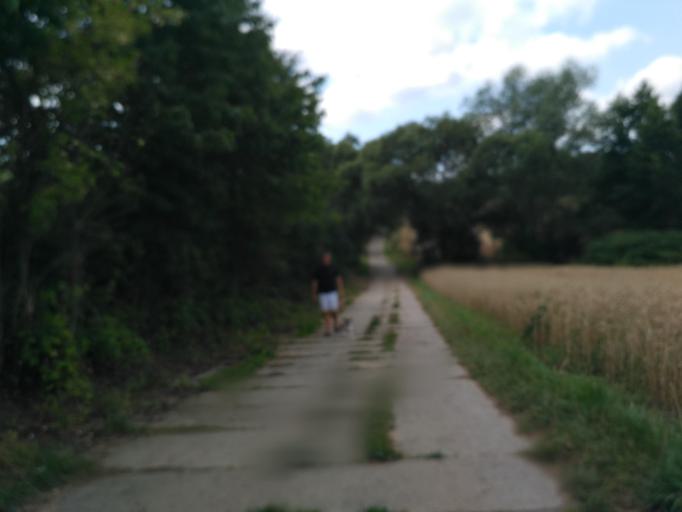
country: PL
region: Subcarpathian Voivodeship
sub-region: Powiat krosnienski
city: Iwonicz-Zdroj
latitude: 49.5942
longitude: 21.7900
